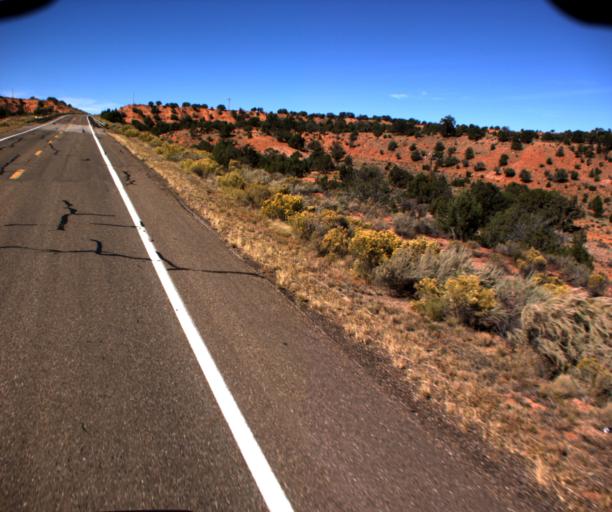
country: US
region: Arizona
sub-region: Mohave County
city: Colorado City
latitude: 36.8799
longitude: -112.8903
